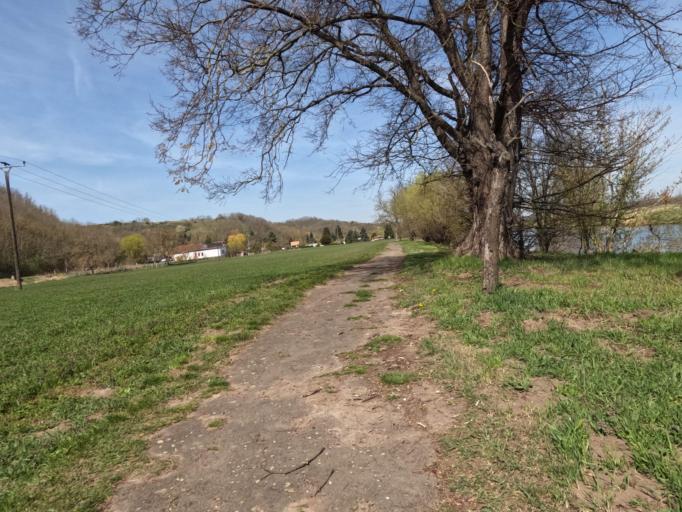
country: DE
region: Saxony-Anhalt
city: Beesenstedt
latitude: 51.5822
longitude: 11.7617
